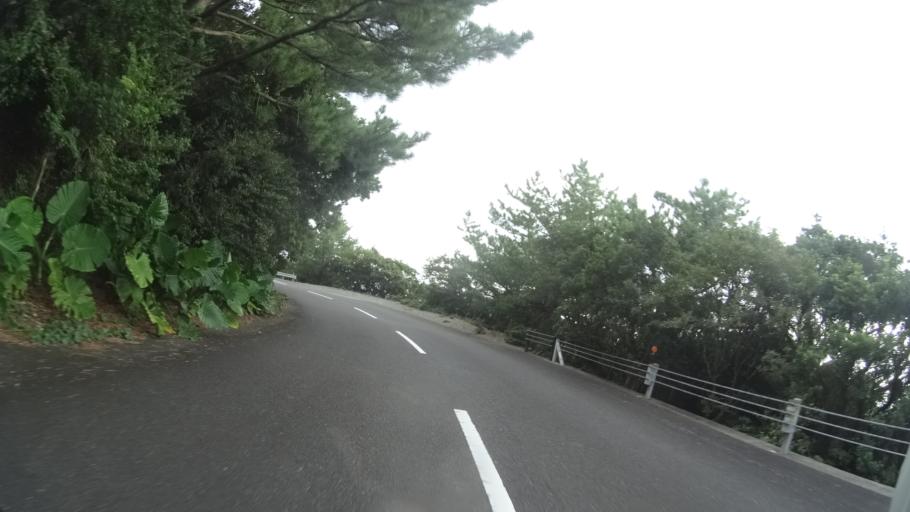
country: JP
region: Kagoshima
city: Nishinoomote
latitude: 30.3216
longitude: 130.3944
